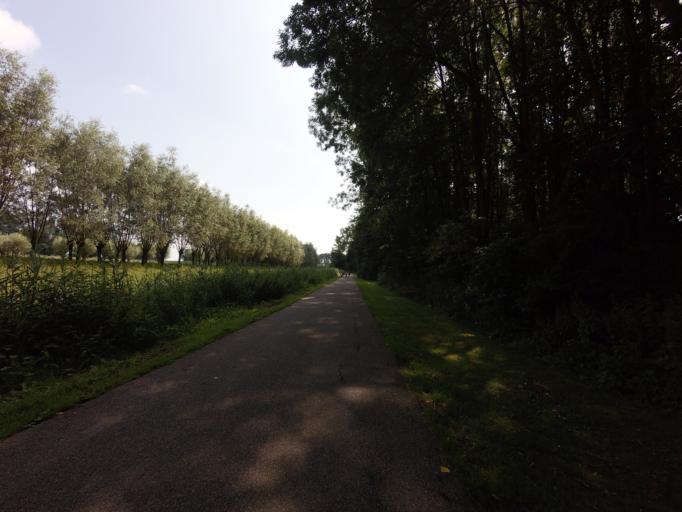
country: NL
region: South Holland
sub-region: Gemeente Sliedrecht
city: Sliedrecht
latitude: 51.8130
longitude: 4.7744
